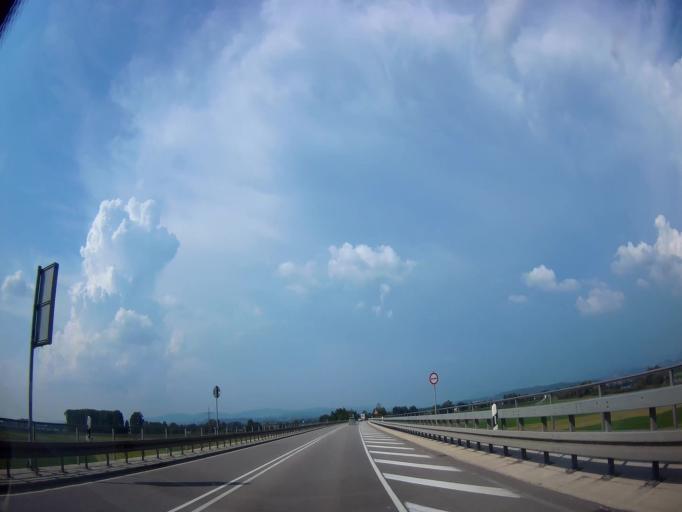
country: DE
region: Bavaria
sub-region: Lower Bavaria
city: Parkstetten
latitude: 48.8986
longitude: 12.6155
